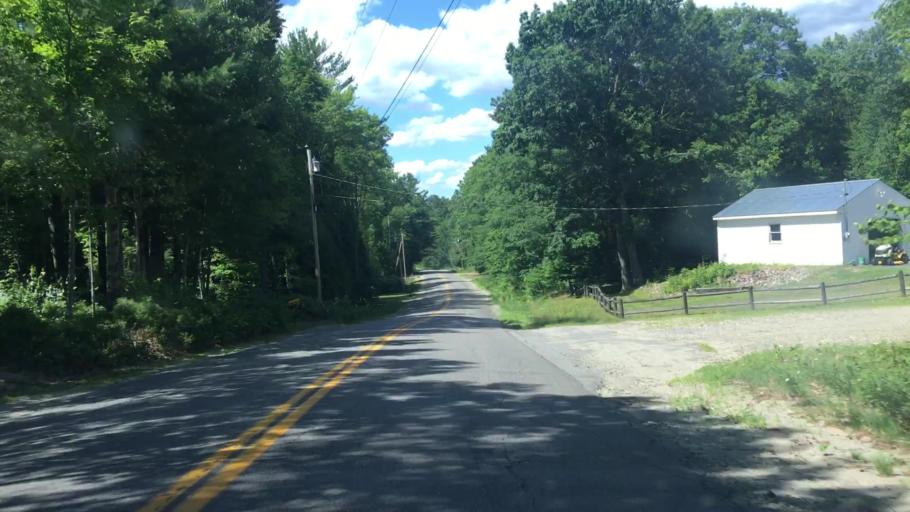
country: US
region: Maine
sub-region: Franklin County
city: Chesterville
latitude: 44.5643
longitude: -70.0864
